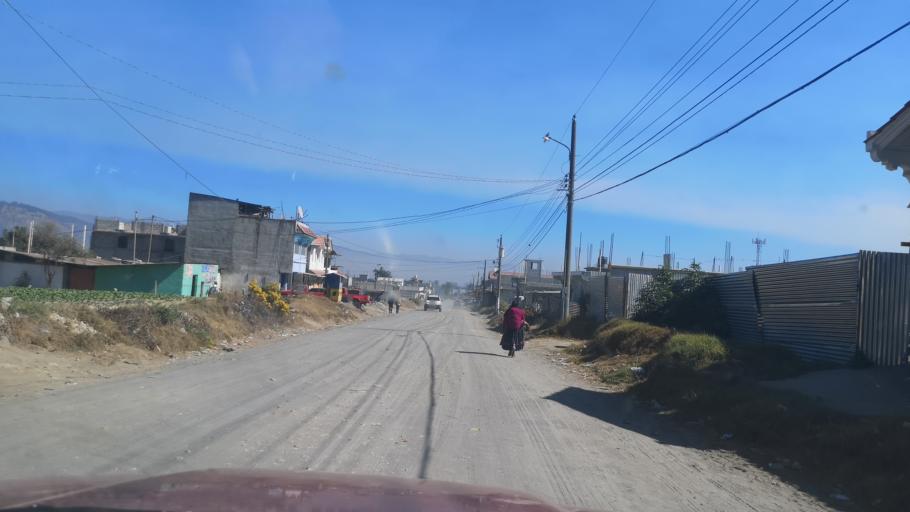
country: GT
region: Quetzaltenango
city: Quetzaltenango
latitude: 14.7927
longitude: -91.5470
